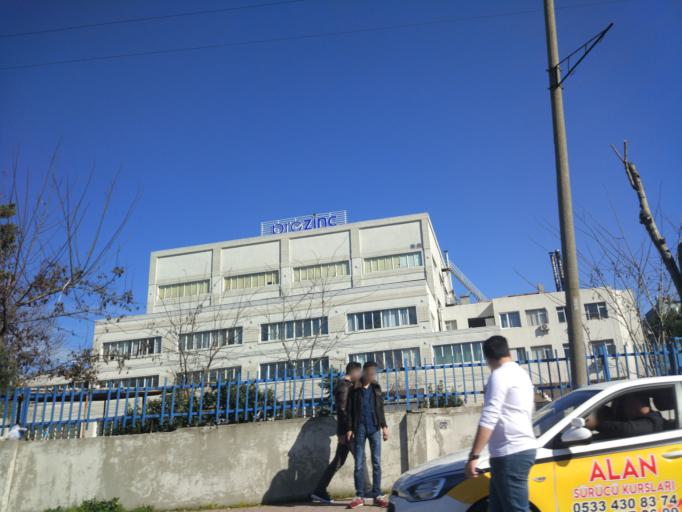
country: TR
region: Istanbul
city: Mahmutbey
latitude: 41.0166
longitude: 28.8134
